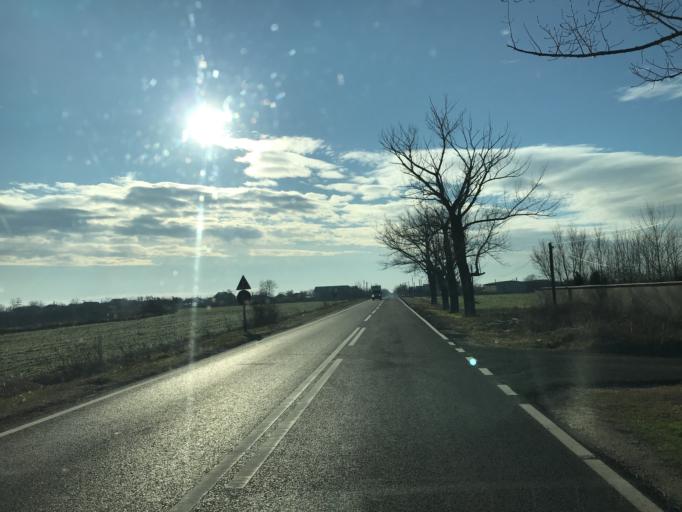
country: RO
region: Olt
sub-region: Comuna Ganeasa
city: Ganeasa
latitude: 44.3928
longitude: 24.2808
